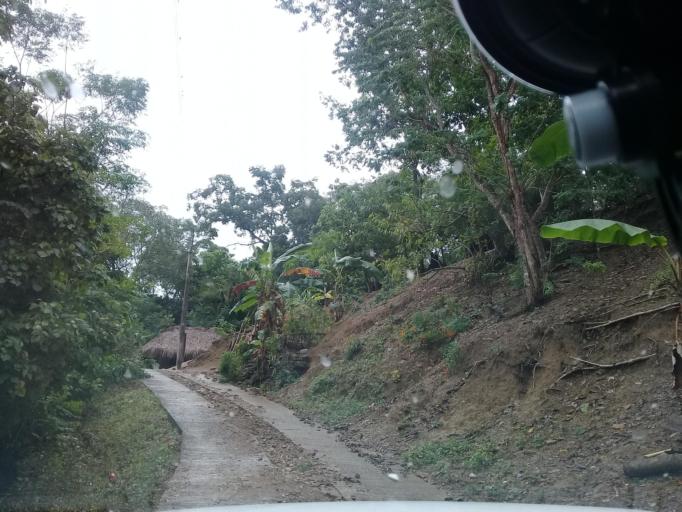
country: MX
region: Veracruz
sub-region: Chalma
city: San Pedro Coyutla
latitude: 21.2371
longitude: -98.4355
